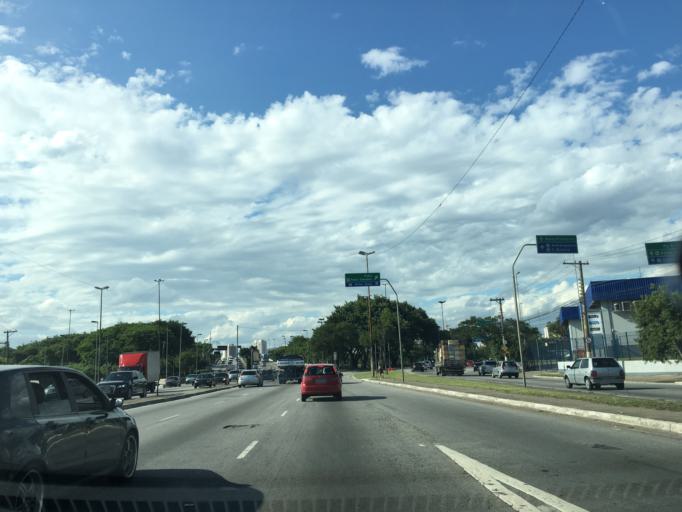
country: BR
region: Sao Paulo
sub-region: Sao Paulo
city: Sao Paulo
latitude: -23.5314
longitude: -46.5832
